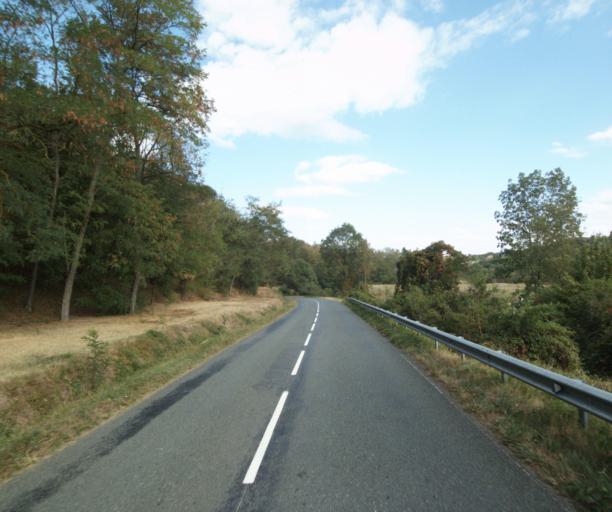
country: FR
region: Rhone-Alpes
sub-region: Departement du Rhone
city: Saint-Germain-Nuelles
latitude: 45.8525
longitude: 4.6408
